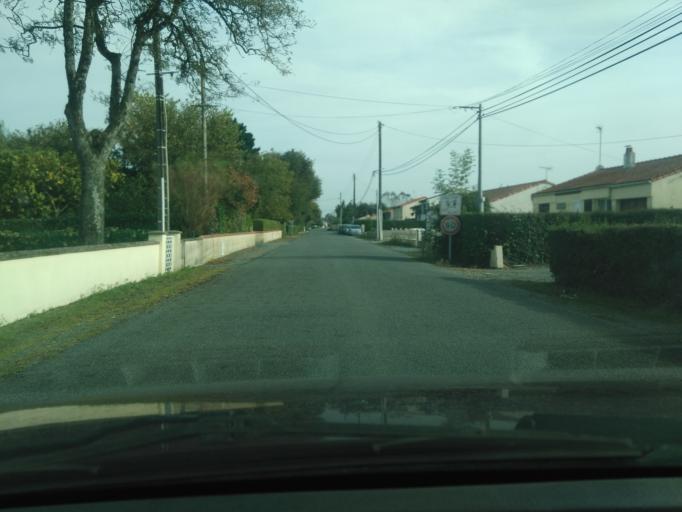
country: FR
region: Pays de la Loire
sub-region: Departement de la Vendee
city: Les Essarts
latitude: 46.7553
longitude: -1.2513
